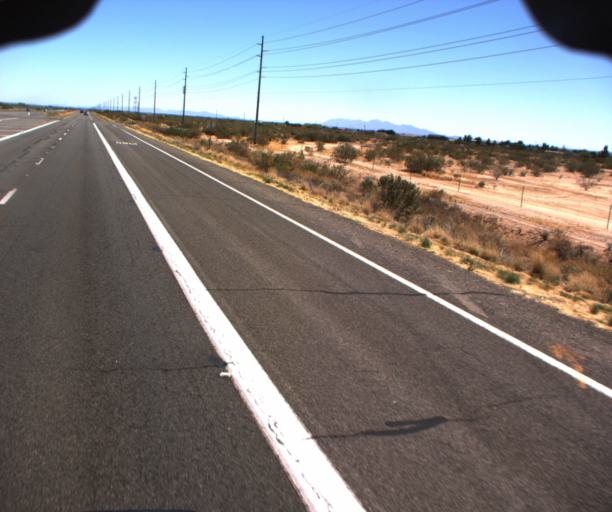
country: US
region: Arizona
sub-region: Maricopa County
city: Sun City West
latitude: 33.7540
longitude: -112.4983
